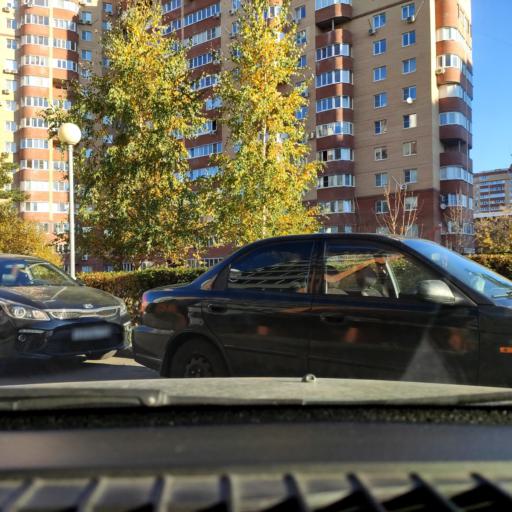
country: RU
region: Samara
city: Tol'yatti
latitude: 53.5378
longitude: 49.3597
